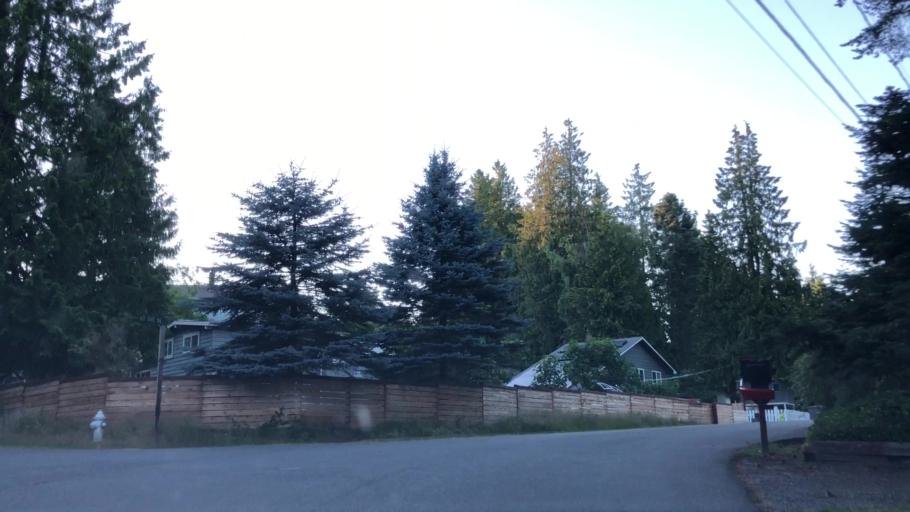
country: US
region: Washington
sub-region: King County
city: Lake Forest Park
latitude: 47.7639
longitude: -122.2649
